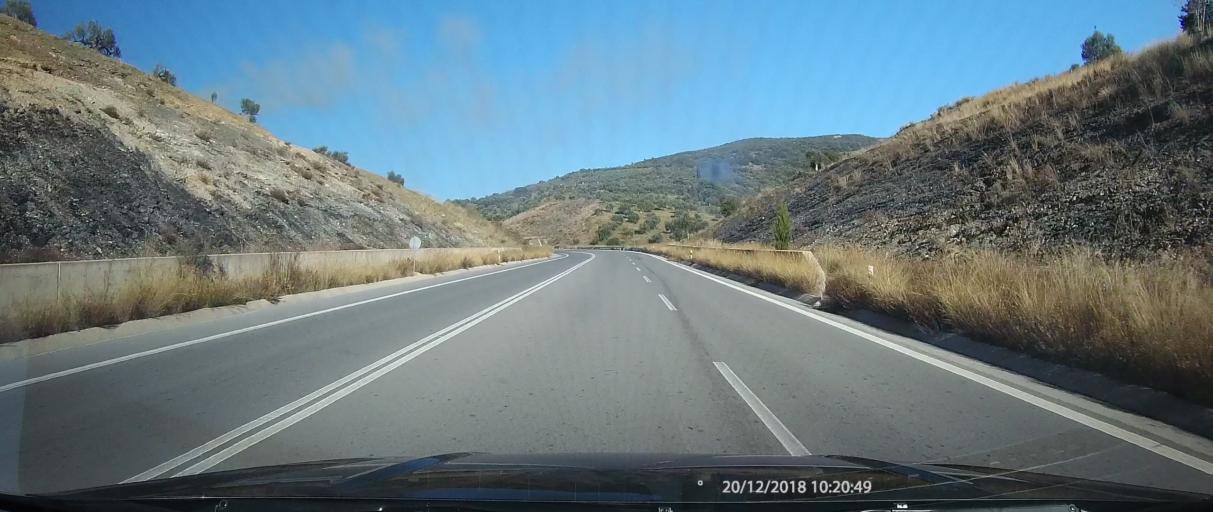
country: GR
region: Peloponnese
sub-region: Nomos Lakonias
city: Magoula
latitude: 37.1528
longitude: 22.4335
